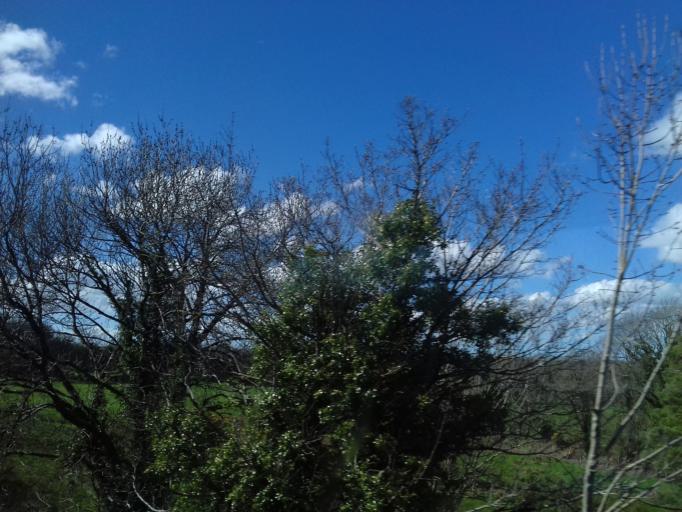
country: IE
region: Munster
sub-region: County Cork
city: Millstreet
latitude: 52.0854
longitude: -9.0217
